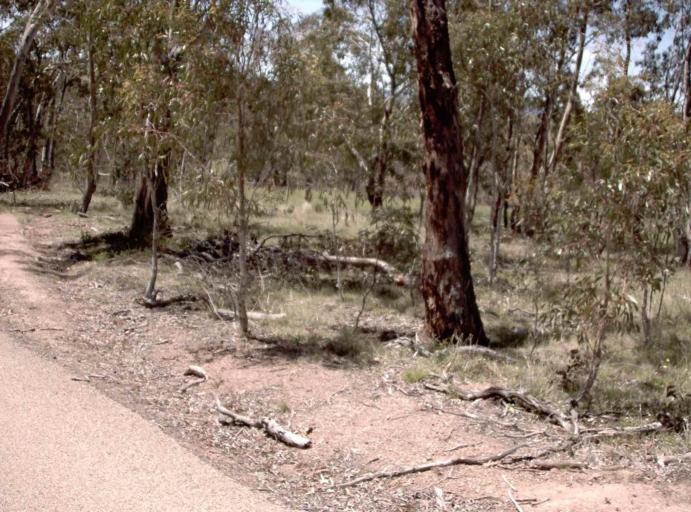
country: AU
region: New South Wales
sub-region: Snowy River
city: Jindabyne
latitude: -37.0509
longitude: 148.2692
